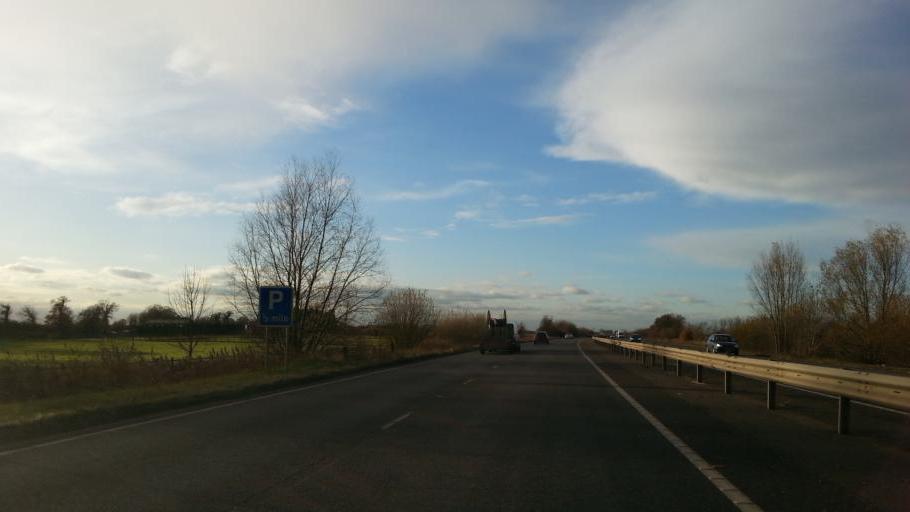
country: GB
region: England
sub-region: Peterborough
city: Thorney
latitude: 52.6219
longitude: -0.0667
